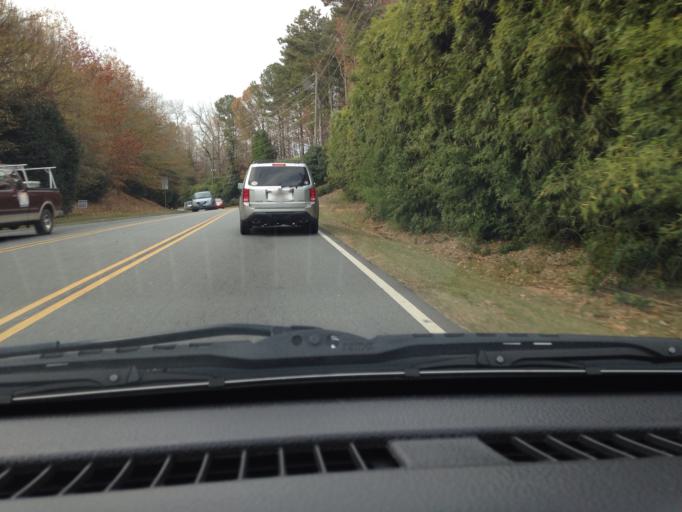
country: US
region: Georgia
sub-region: Fulton County
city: Johns Creek
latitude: 34.0859
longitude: -84.1900
